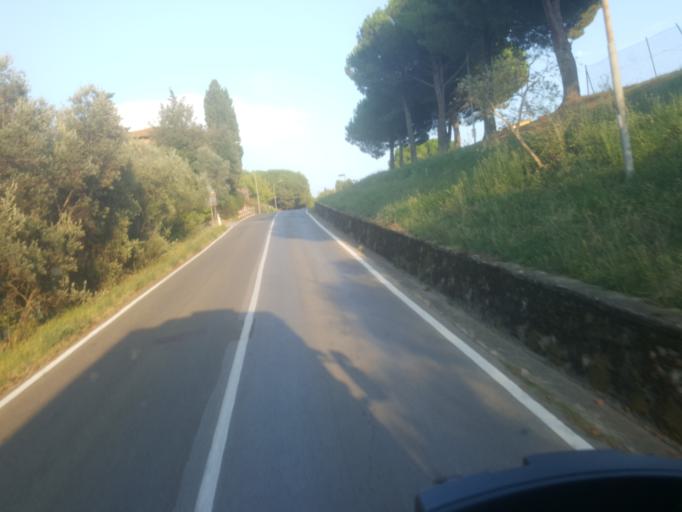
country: IT
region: Tuscany
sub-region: Province of Florence
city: Montaione
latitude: 43.5474
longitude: 10.9213
